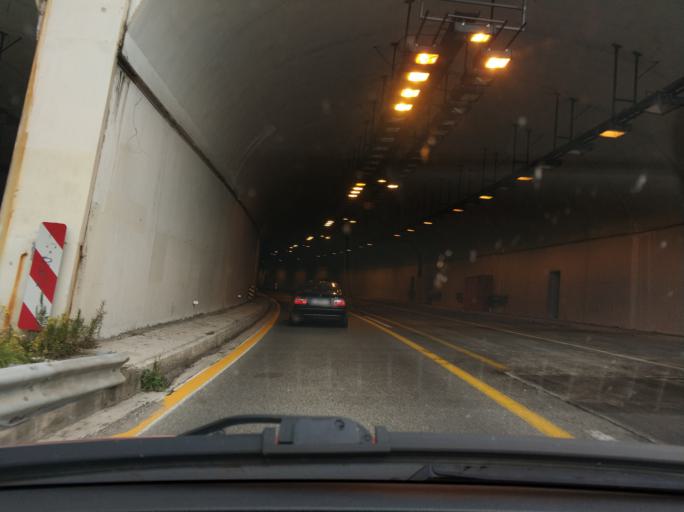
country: GR
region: East Macedonia and Thrace
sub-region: Nomos Kavalas
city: Palaio Tsifliki
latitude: 40.9098
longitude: 24.3557
